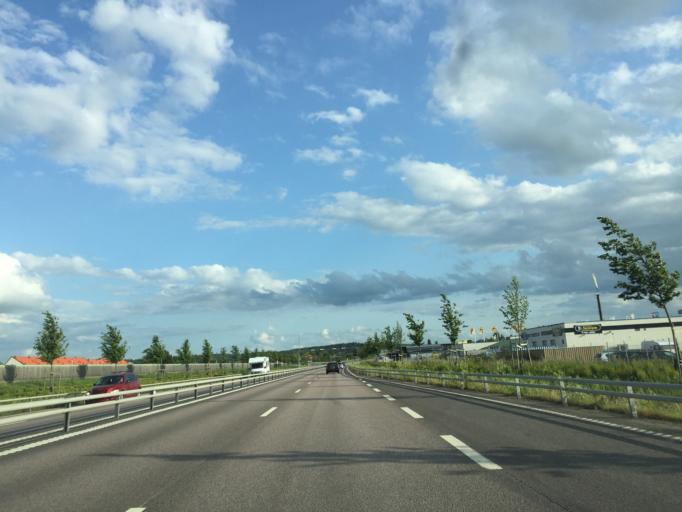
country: SE
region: OEstergoetland
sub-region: Motala Kommun
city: Motala
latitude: 58.5413
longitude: 15.0165
